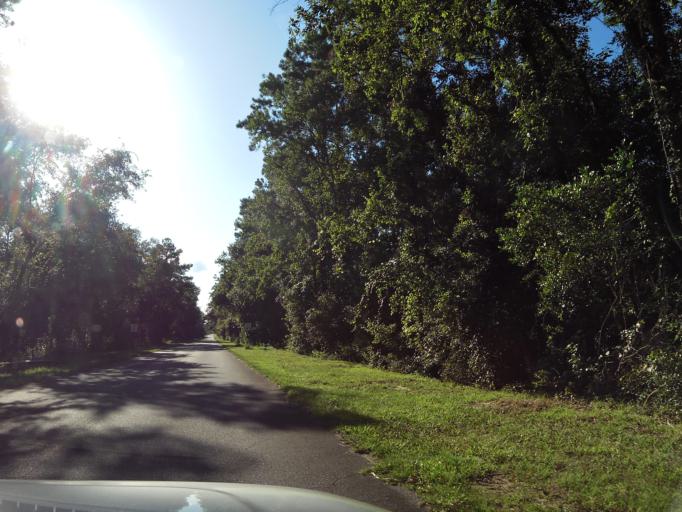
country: US
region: Florida
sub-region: Wakulla County
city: Crawfordville
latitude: 30.0630
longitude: -84.5013
